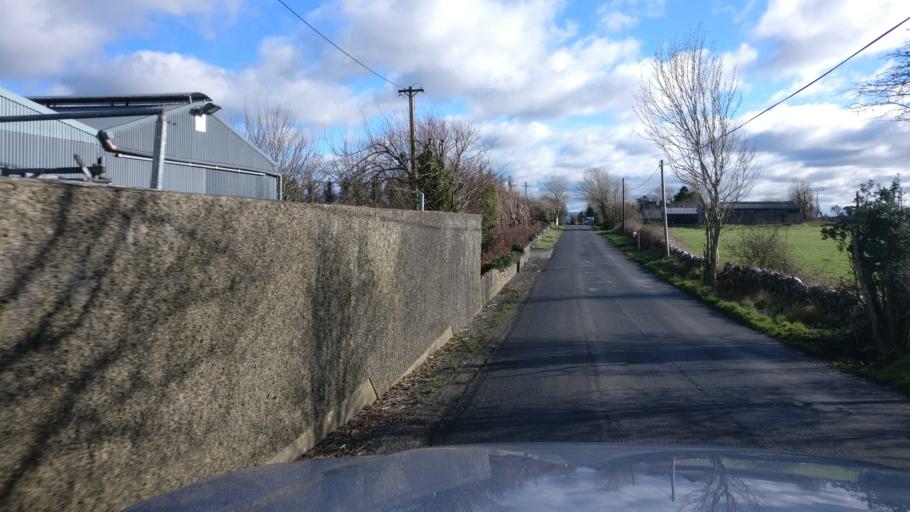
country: IE
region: Connaught
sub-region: County Galway
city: Oranmore
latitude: 53.2610
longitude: -8.8629
